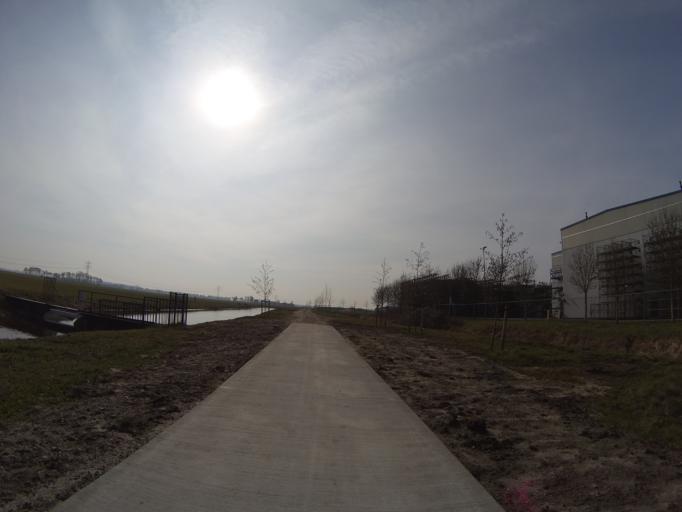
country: NL
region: Utrecht
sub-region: Gemeente Bunschoten
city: Bunschoten
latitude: 52.2262
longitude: 5.3815
